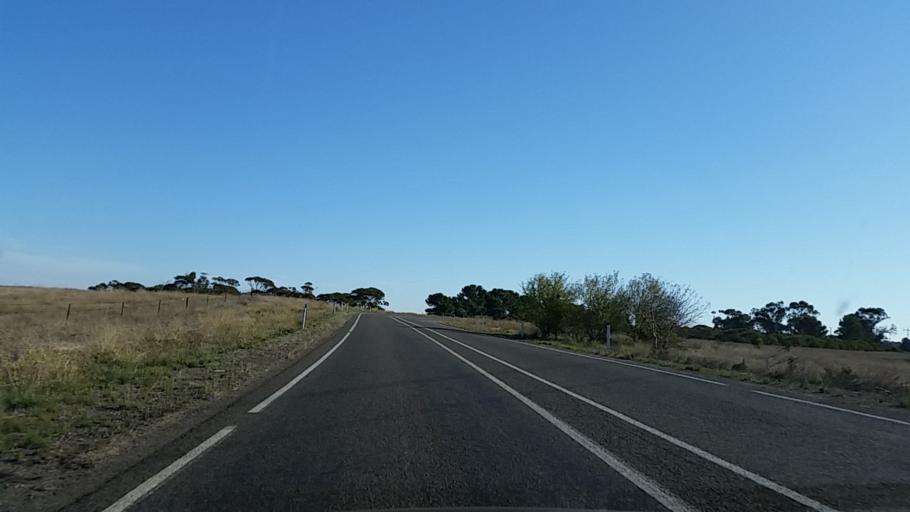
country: AU
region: South Australia
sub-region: Mount Barker
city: Callington
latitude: -35.1192
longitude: 139.1573
